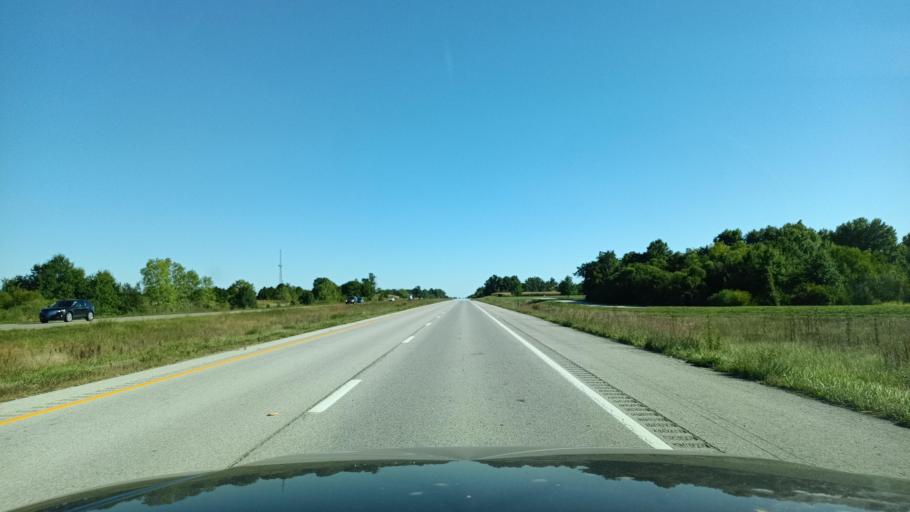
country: US
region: Missouri
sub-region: Randolph County
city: Moberly
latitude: 39.3604
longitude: -92.4025
